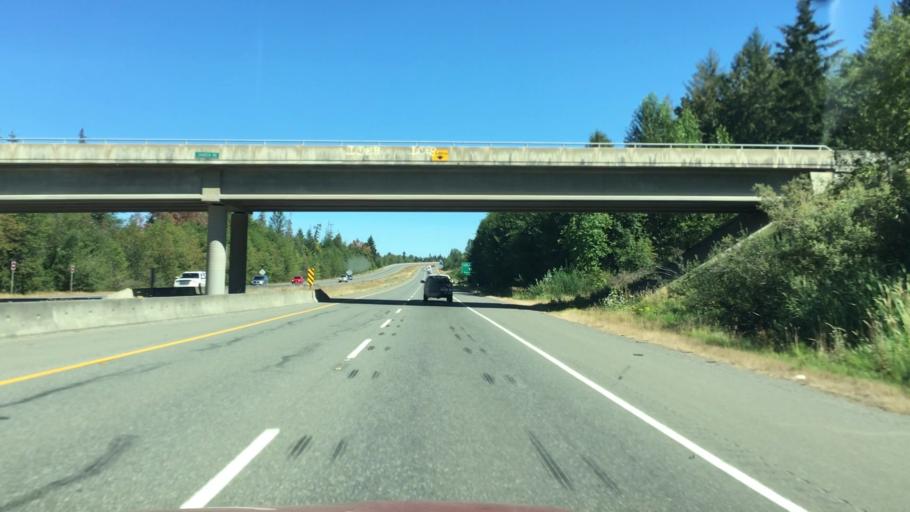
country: CA
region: British Columbia
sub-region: Regional District of Nanaimo
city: Parksville
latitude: 49.3143
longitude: -124.3575
